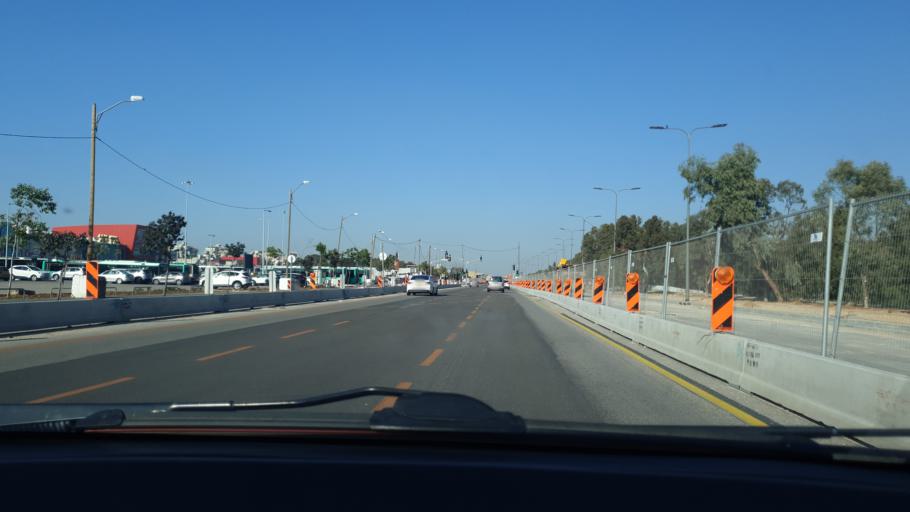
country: IL
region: Tel Aviv
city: Holon
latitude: 31.9887
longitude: 34.7766
